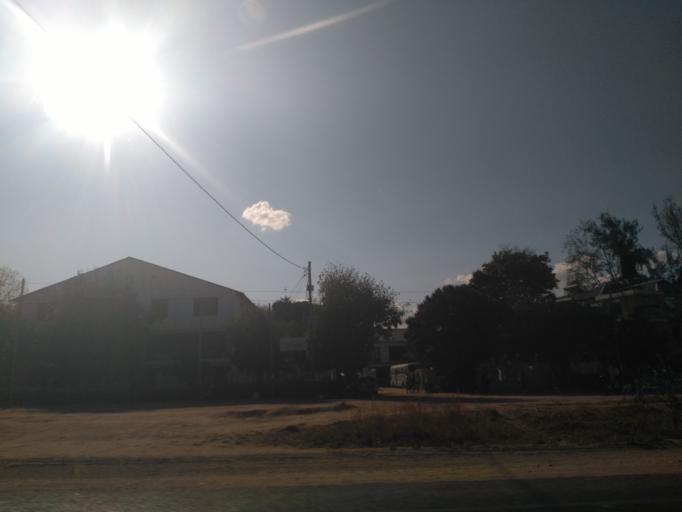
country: TZ
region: Dodoma
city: Dodoma
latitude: -6.1642
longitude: 35.7463
